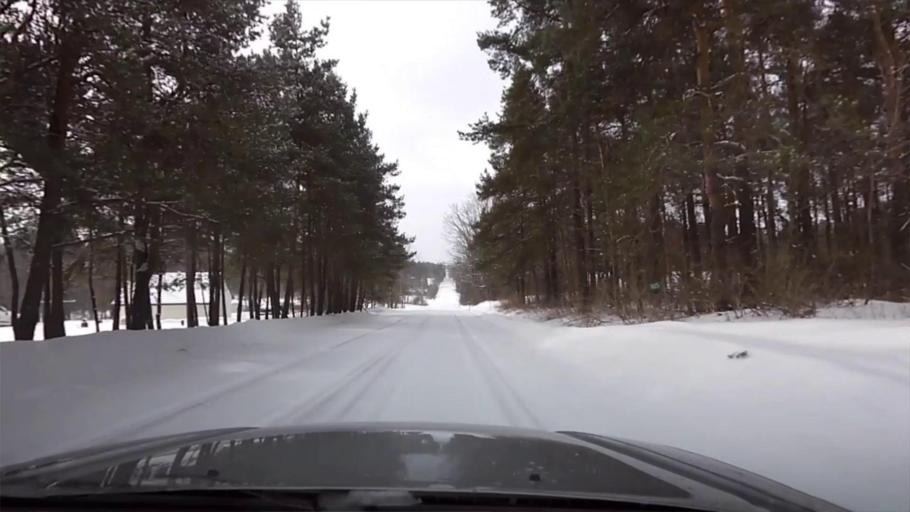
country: US
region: New York
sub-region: Cattaraugus County
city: Franklinville
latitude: 42.3308
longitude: -78.3540
